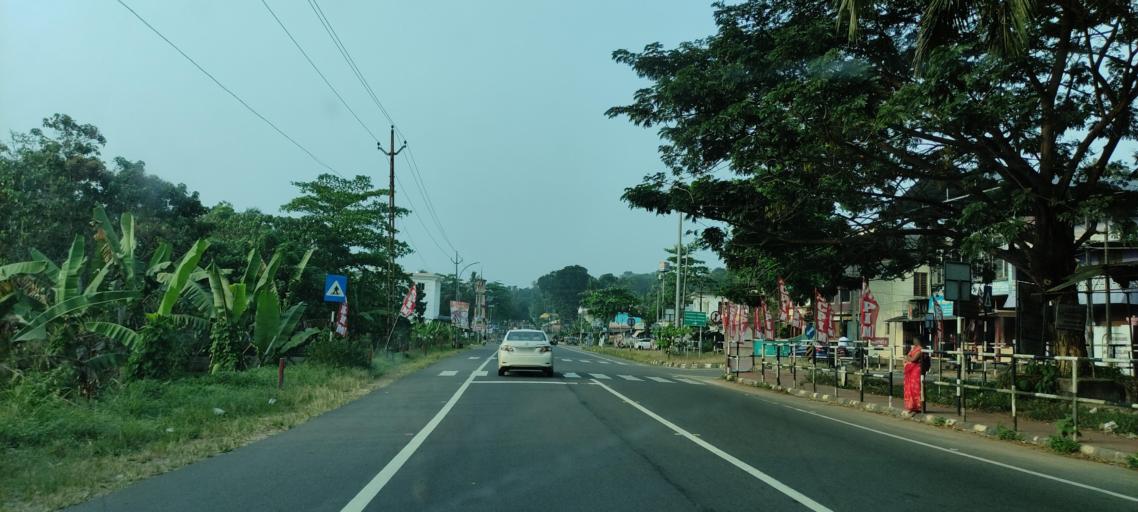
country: IN
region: Kerala
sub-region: Pattanamtitta
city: Adur
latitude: 9.0954
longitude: 76.7527
